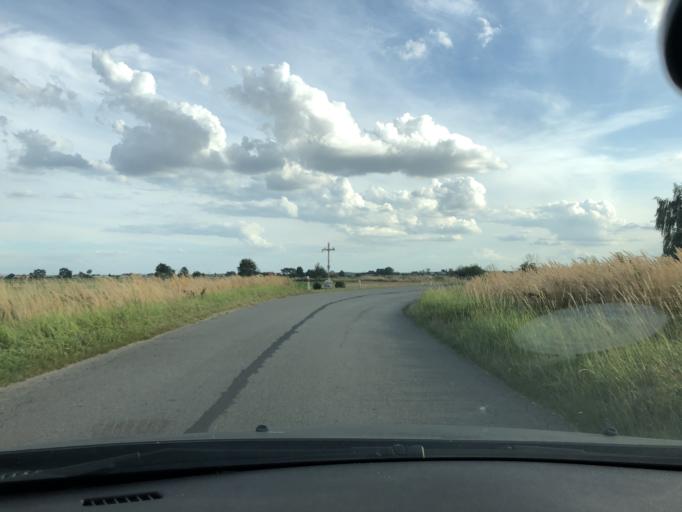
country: PL
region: Lodz Voivodeship
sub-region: Powiat wieruszowski
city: Walichnowy
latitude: 51.2574
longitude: 18.3943
